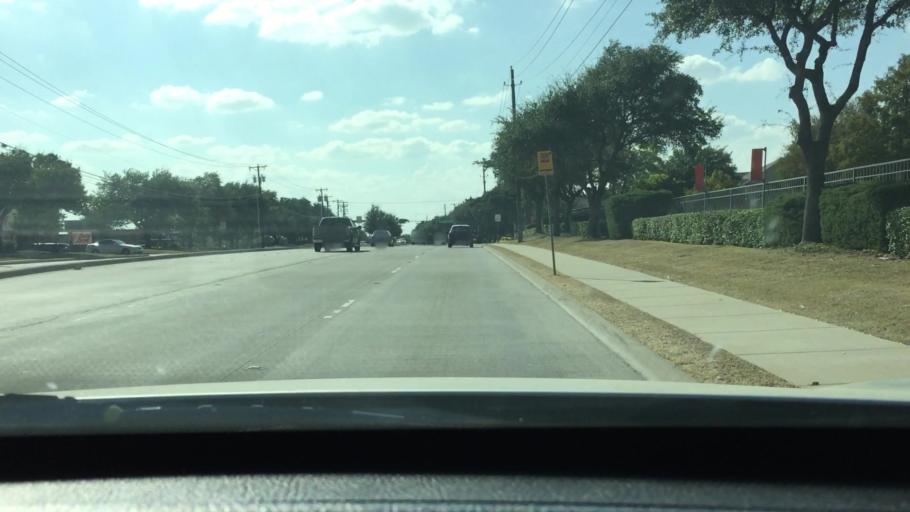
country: US
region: Texas
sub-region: Dallas County
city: Addison
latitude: 32.9873
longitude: -96.8447
